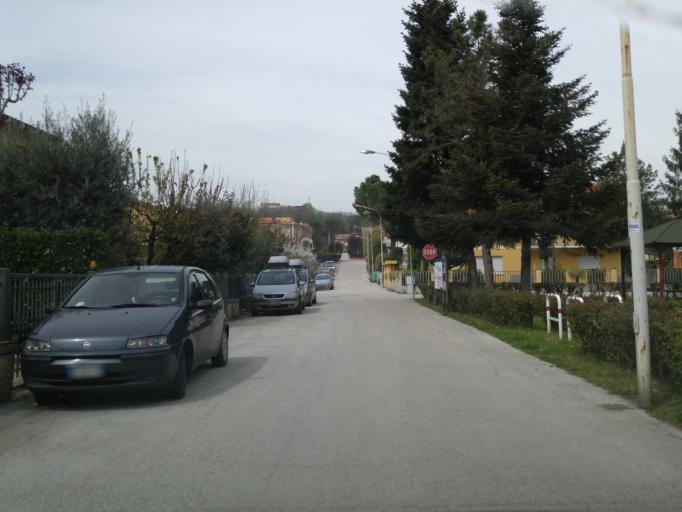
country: IT
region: The Marches
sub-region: Provincia di Pesaro e Urbino
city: Tavernelle
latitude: 43.7358
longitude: 12.8987
